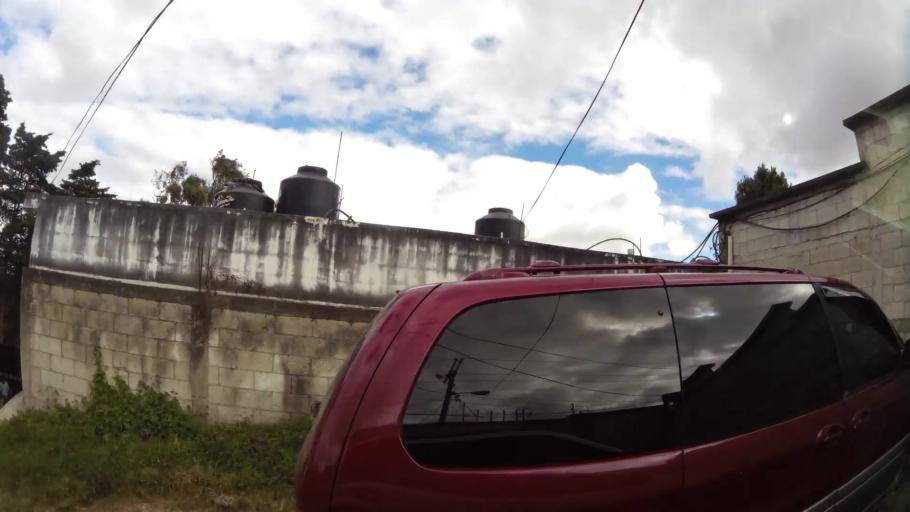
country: GT
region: Guatemala
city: Mixco
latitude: 14.6351
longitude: -90.6058
